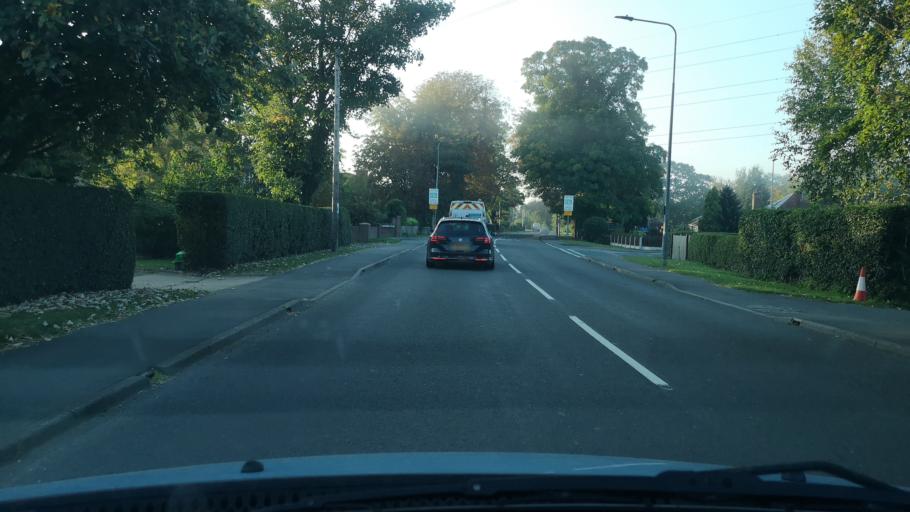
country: GB
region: England
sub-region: North Lincolnshire
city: Crowle
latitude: 53.6012
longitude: -0.8282
